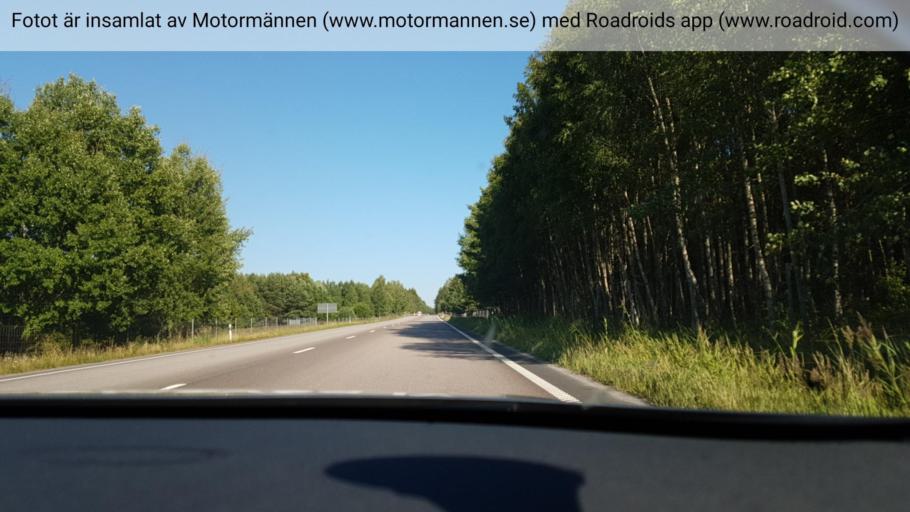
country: SE
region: Vaestra Goetaland
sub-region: Lidkopings Kommun
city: Vinninga
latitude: 58.4306
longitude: 13.2981
